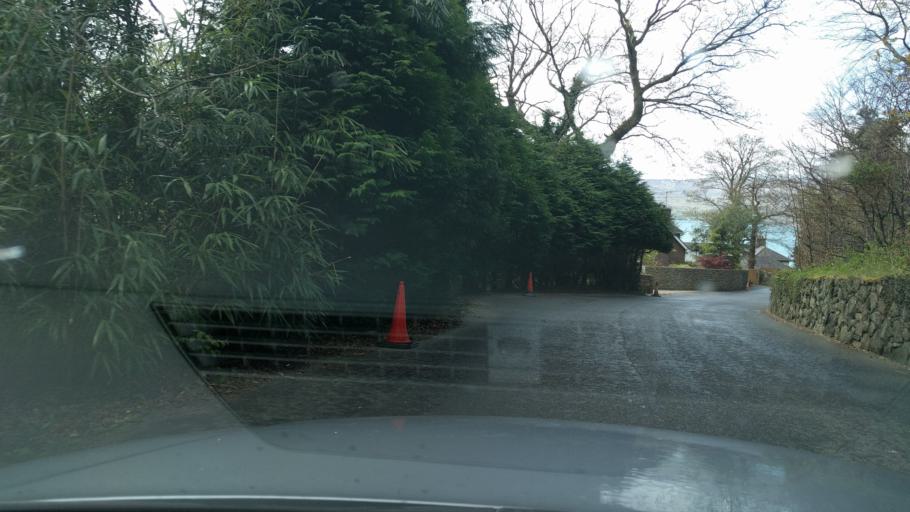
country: GB
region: Northern Ireland
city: Rostrevor
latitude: 54.0952
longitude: -6.1895
